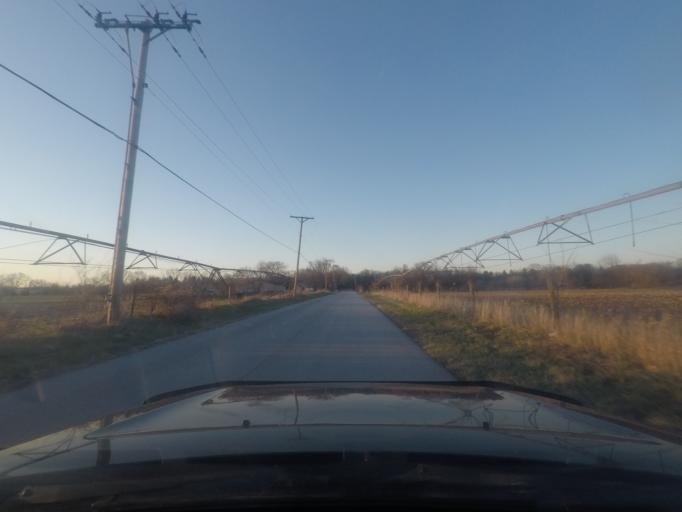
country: US
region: Indiana
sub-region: LaPorte County
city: Kingsford Heights
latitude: 41.5109
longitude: -86.6977
